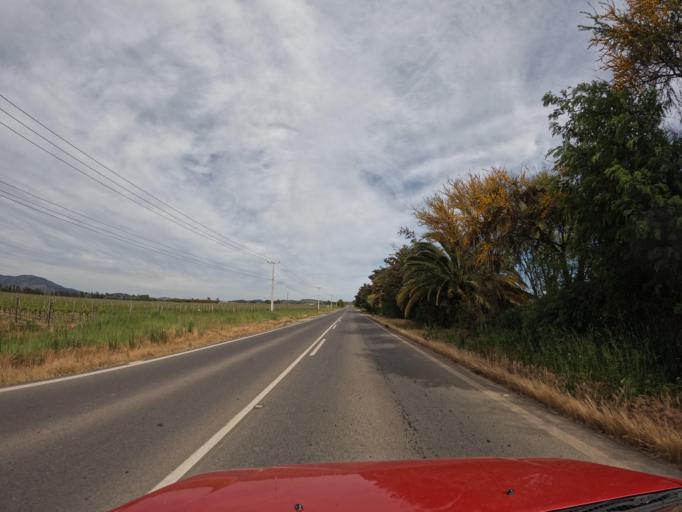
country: CL
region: Maule
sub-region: Provincia de Talca
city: Talca
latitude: -35.3810
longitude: -71.8251
